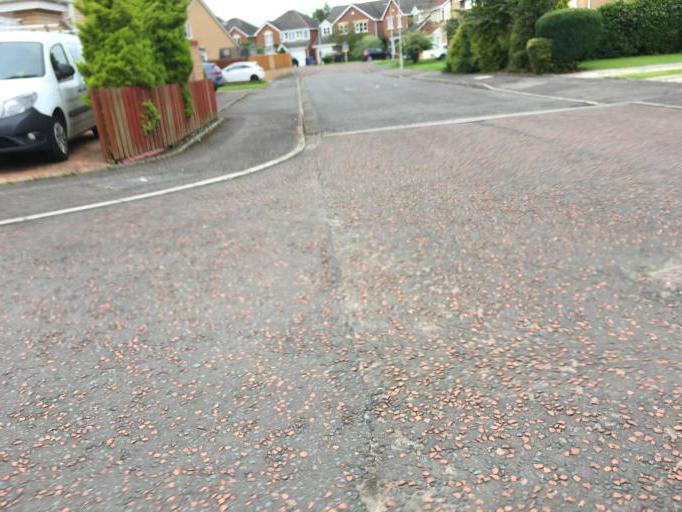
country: GB
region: Scotland
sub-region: West Lothian
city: Livingston
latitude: 55.8669
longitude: -3.5101
